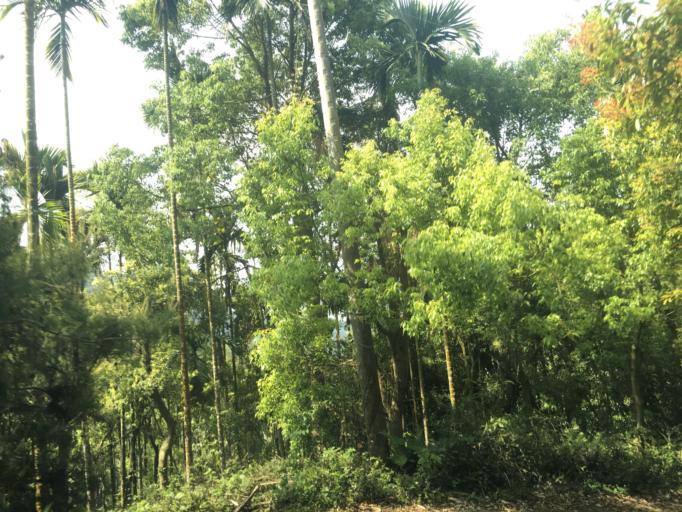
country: TW
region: Taiwan
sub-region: Taichung City
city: Taichung
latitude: 24.1315
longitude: 120.8241
